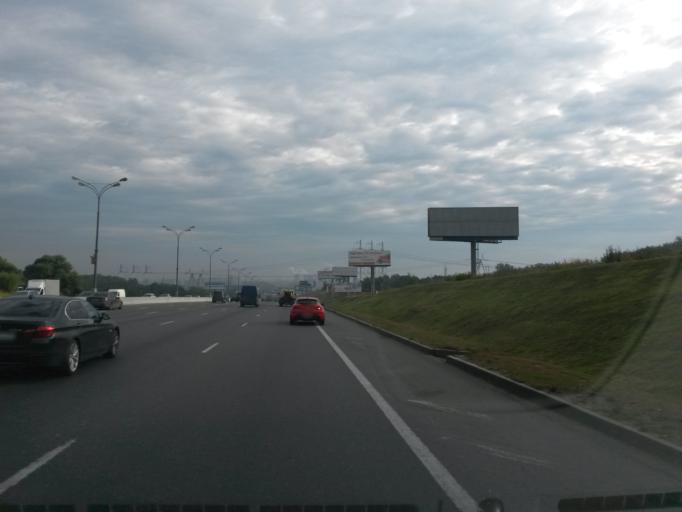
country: RU
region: Moscow
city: Zyablikovo
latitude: 55.6102
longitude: 37.7689
